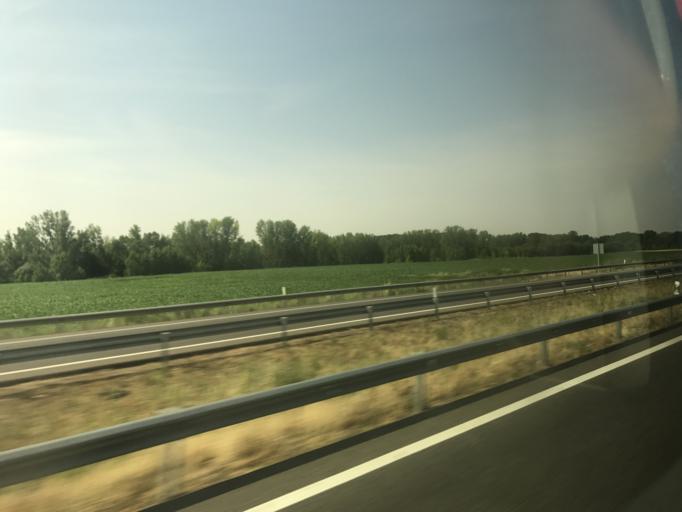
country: ES
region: Castille and Leon
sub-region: Provincia de Palencia
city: Quintana del Puente
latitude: 42.1034
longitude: -4.1891
